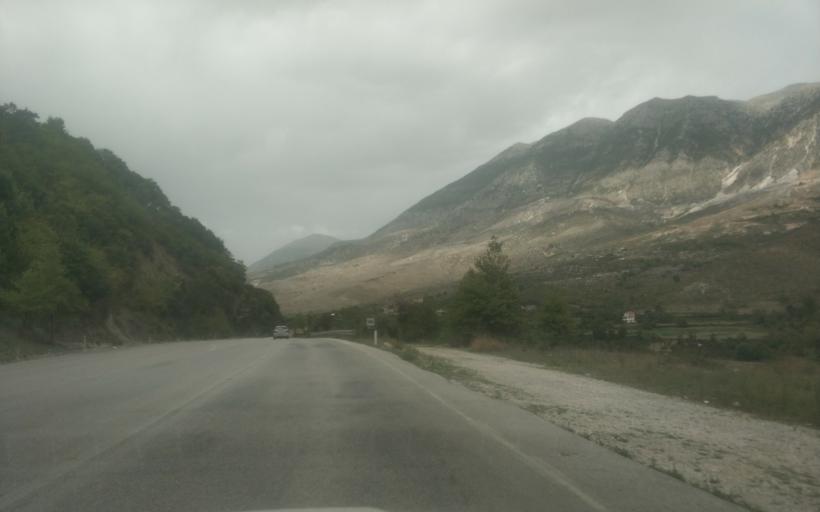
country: AL
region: Gjirokaster
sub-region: Rrethi i Gjirokastres
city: Picar
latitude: 40.2257
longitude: 20.0859
